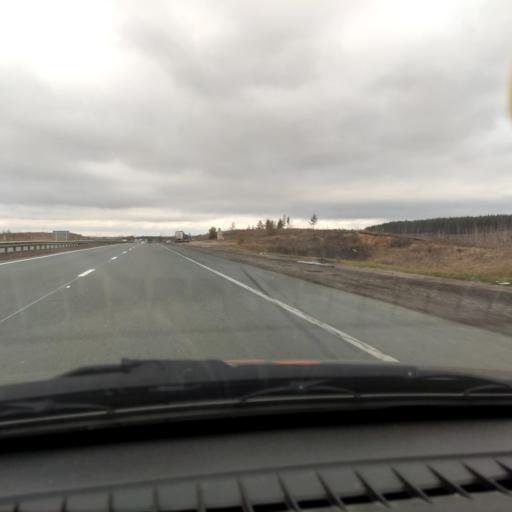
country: RU
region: Samara
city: Zhigulevsk
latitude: 53.5051
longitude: 49.5386
